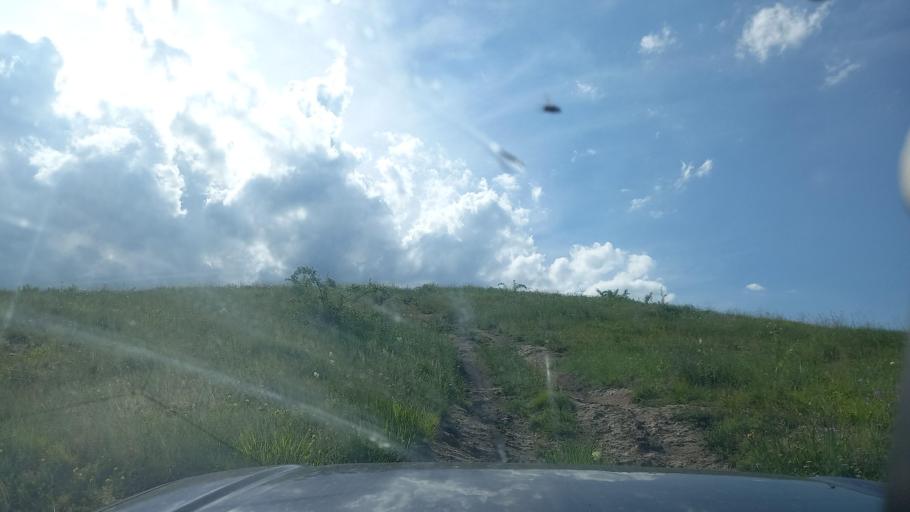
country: RU
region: Karachayevo-Cherkesiya
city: Pregradnaya
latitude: 44.1232
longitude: 41.1004
